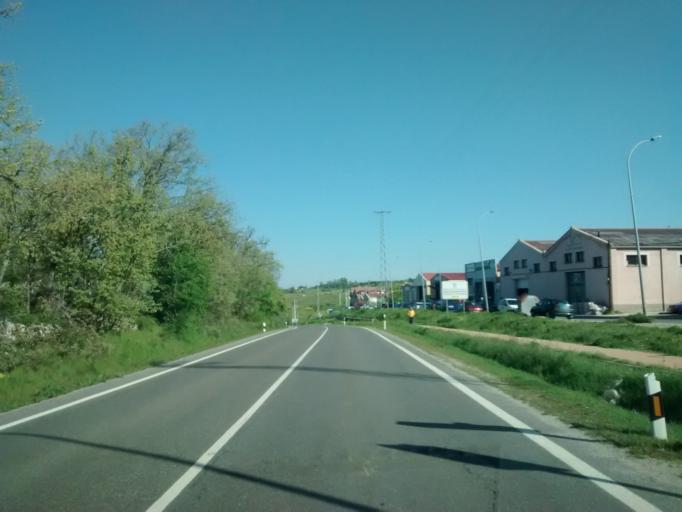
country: ES
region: Castille and Leon
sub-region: Provincia de Segovia
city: San Ildefonso
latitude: 40.9095
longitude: -4.0099
